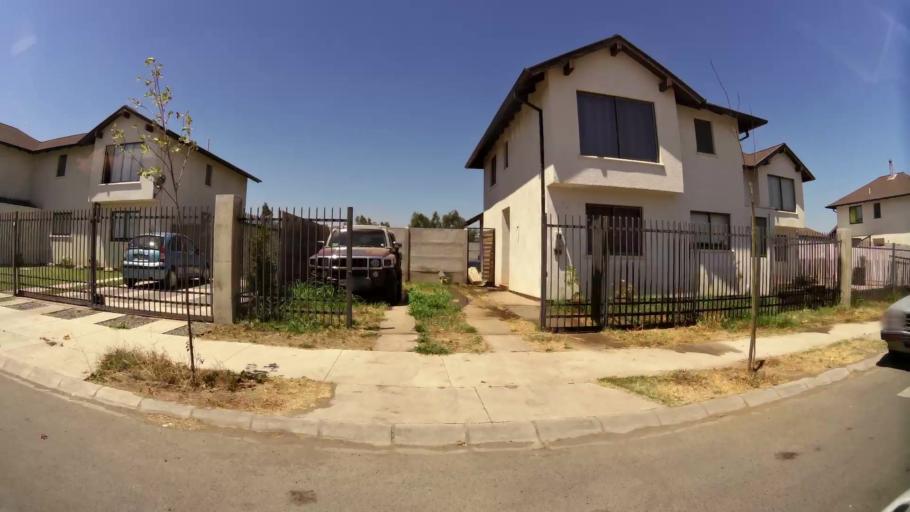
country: CL
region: Maule
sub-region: Provincia de Curico
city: Curico
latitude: -34.9858
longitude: -71.2125
